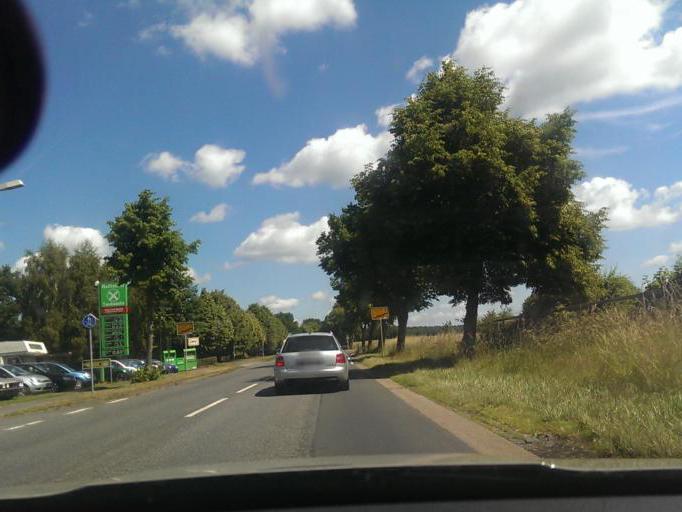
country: DE
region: Lower Saxony
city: Verden
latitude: 52.9784
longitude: 9.2582
